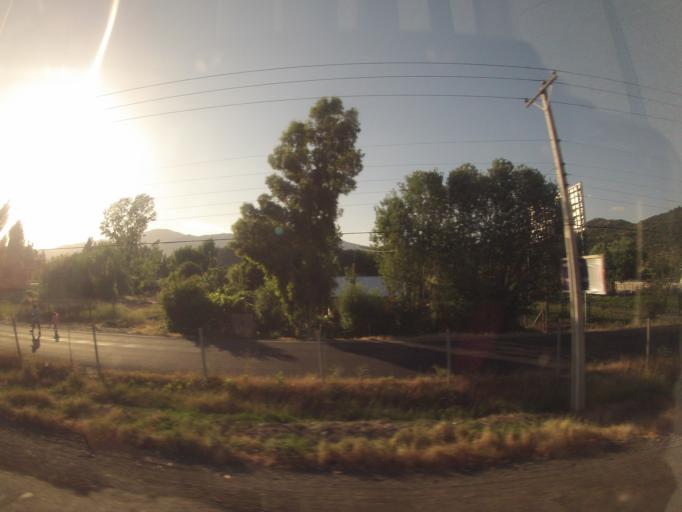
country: CL
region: O'Higgins
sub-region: Provincia de Cachapoal
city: Rengo
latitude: -34.5292
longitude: -70.9376
